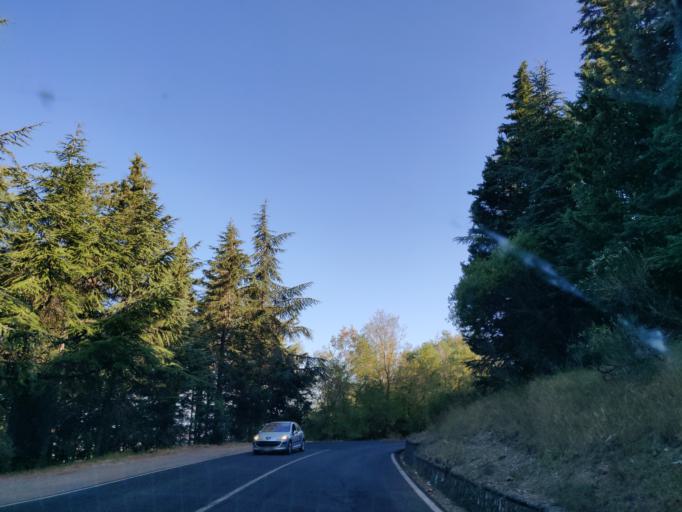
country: IT
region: Tuscany
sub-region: Provincia di Siena
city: Abbadia San Salvatore
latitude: 42.8729
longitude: 11.6835
